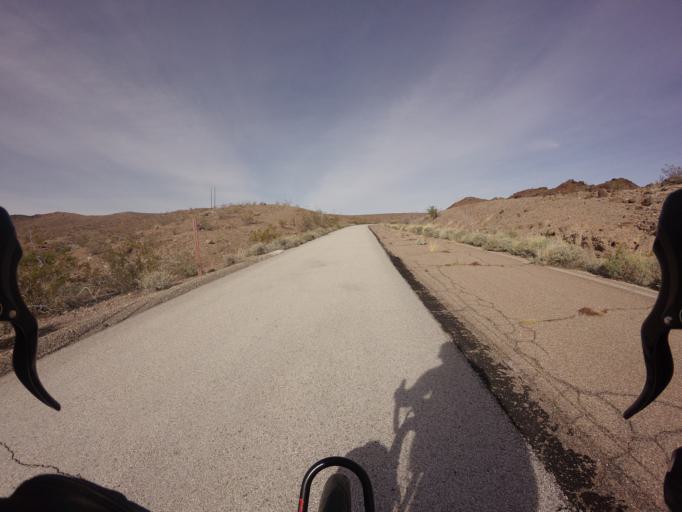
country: US
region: Nevada
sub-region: Clark County
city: Boulder City
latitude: 36.0839
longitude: -114.8296
